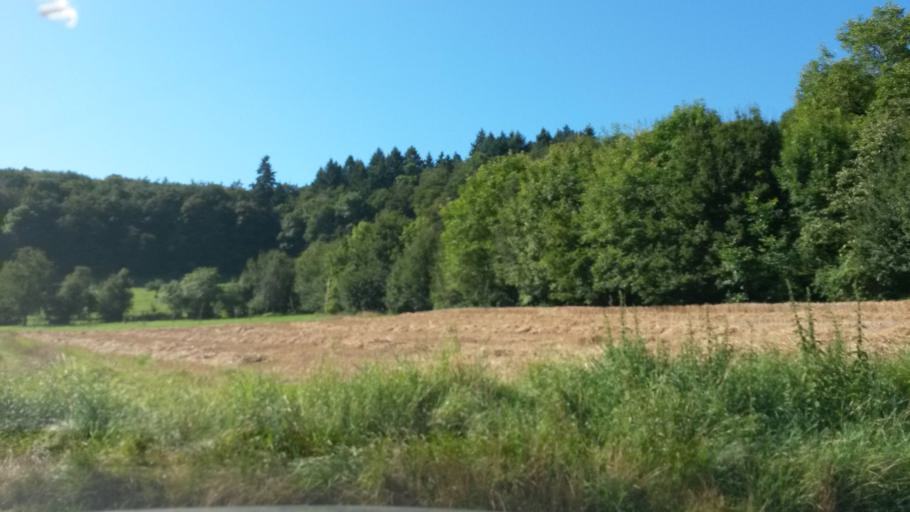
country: DE
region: Baden-Wuerttemberg
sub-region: Karlsruhe Region
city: Konigsbach-Stein
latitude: 48.9580
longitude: 8.6353
